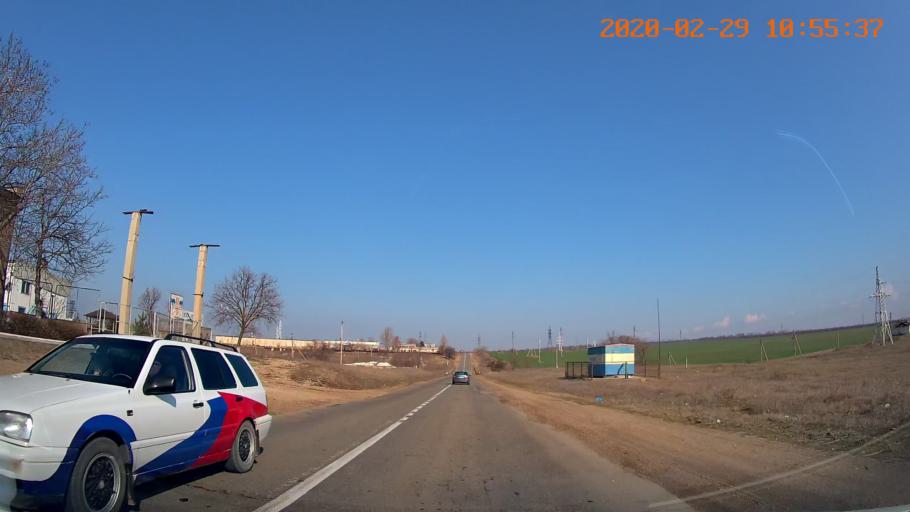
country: MD
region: Telenesti
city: Grigoriopol
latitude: 47.1358
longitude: 29.3253
